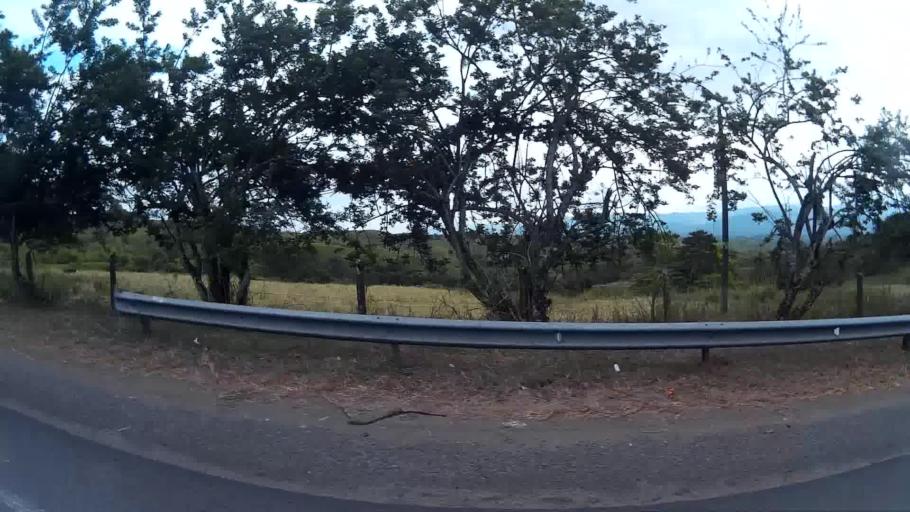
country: CO
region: Risaralda
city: La Virginia
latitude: 4.8524
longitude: -75.8668
